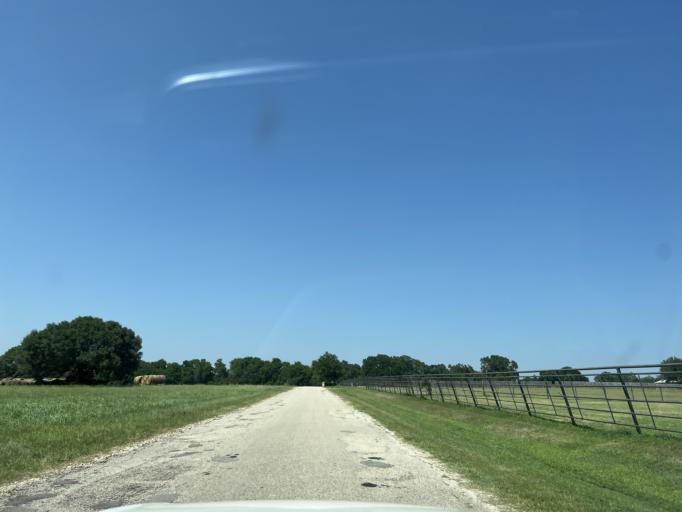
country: US
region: Texas
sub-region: Washington County
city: Brenham
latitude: 30.1762
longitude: -96.4961
